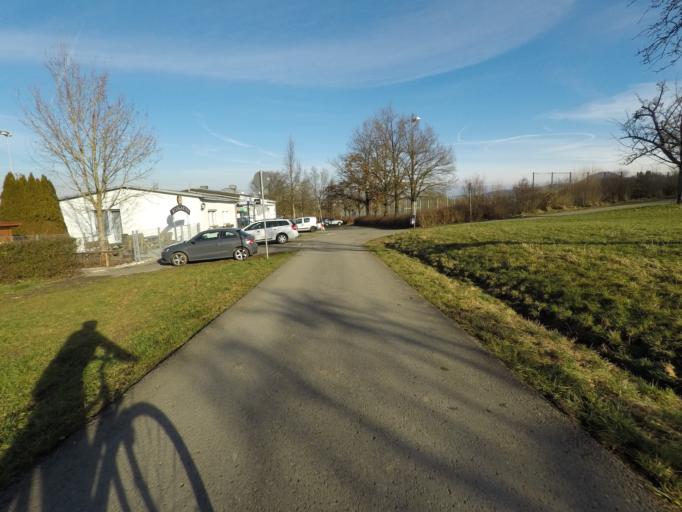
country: DE
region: Baden-Wuerttemberg
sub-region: Tuebingen Region
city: Wannweil
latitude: 48.4928
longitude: 9.1681
